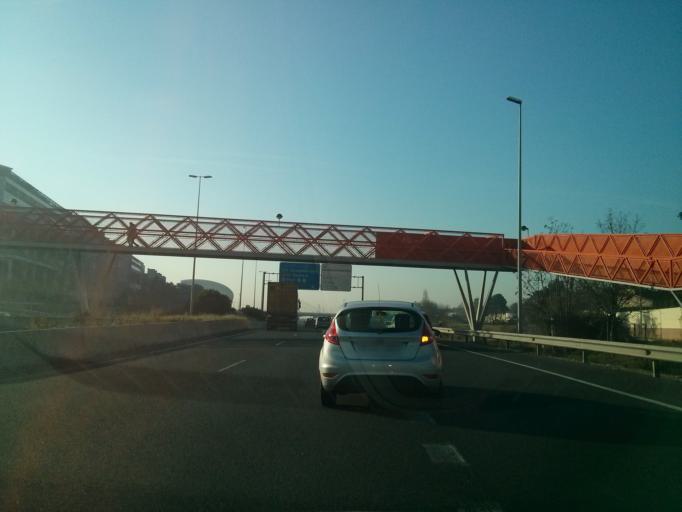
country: ES
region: Valencia
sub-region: Provincia de Valencia
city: Paterna
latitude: 39.5066
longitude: -0.4328
